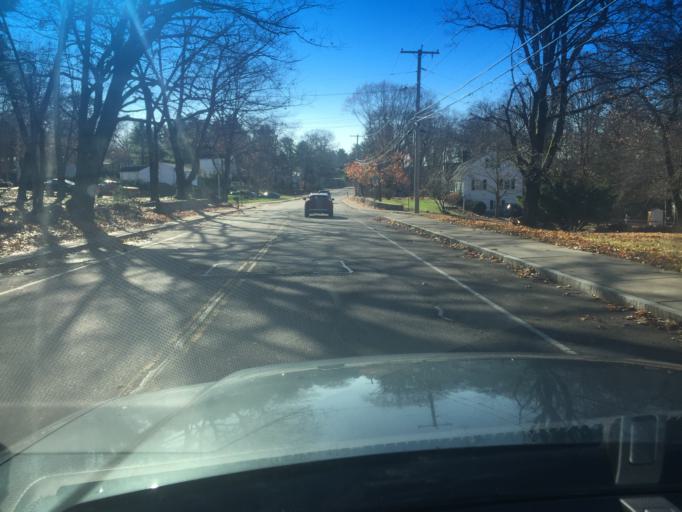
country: US
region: Massachusetts
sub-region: Norfolk County
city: Franklin
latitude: 42.0975
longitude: -71.4273
